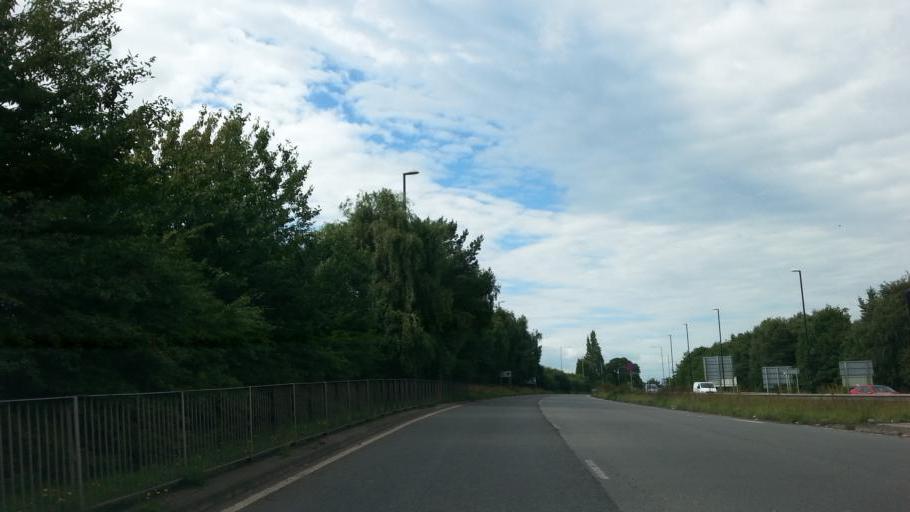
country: GB
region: England
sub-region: Warwickshire
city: Exhall
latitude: 52.4495
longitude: -1.4999
